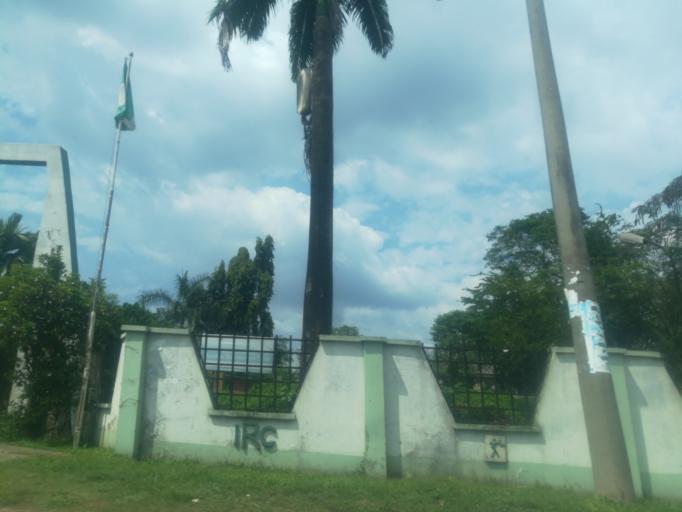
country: NG
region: Oyo
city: Ibadan
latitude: 7.3994
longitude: 3.8849
